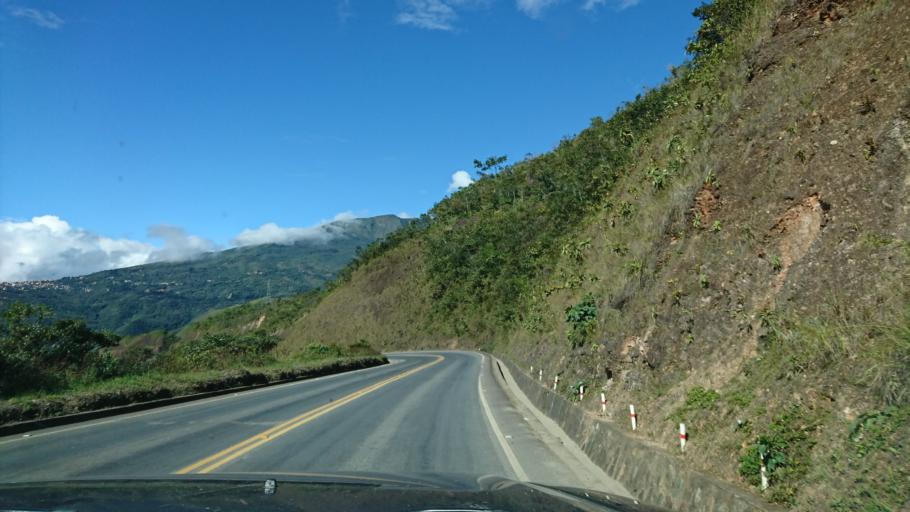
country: BO
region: La Paz
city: Coroico
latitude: -16.2052
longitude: -67.7723
